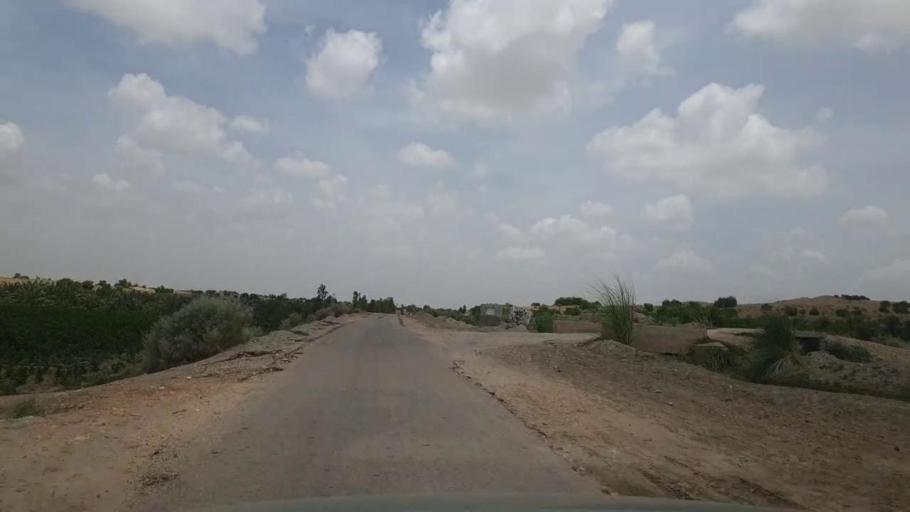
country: PK
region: Sindh
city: Kot Diji
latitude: 27.1983
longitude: 69.0669
